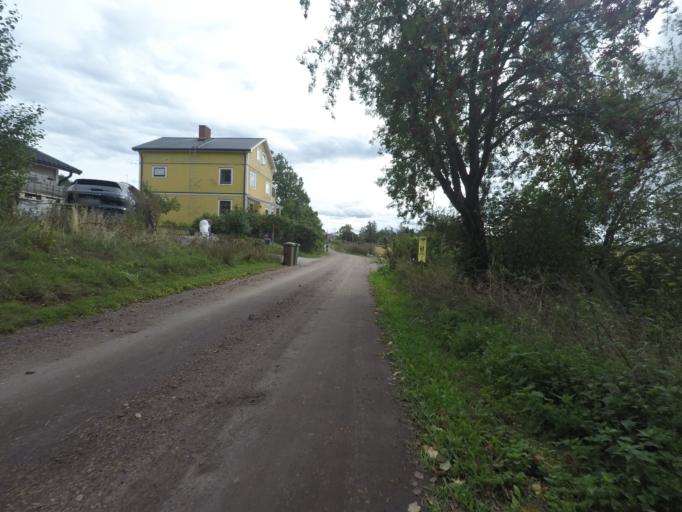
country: SE
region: Vaestmanland
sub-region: Kungsors Kommun
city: Kungsoer
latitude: 59.4581
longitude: 16.0727
